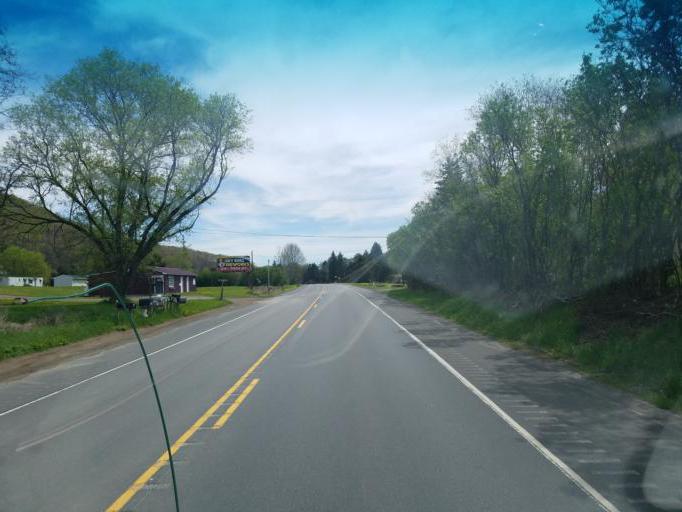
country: US
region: Pennsylvania
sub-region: Potter County
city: Galeton
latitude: 41.7457
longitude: -77.5949
